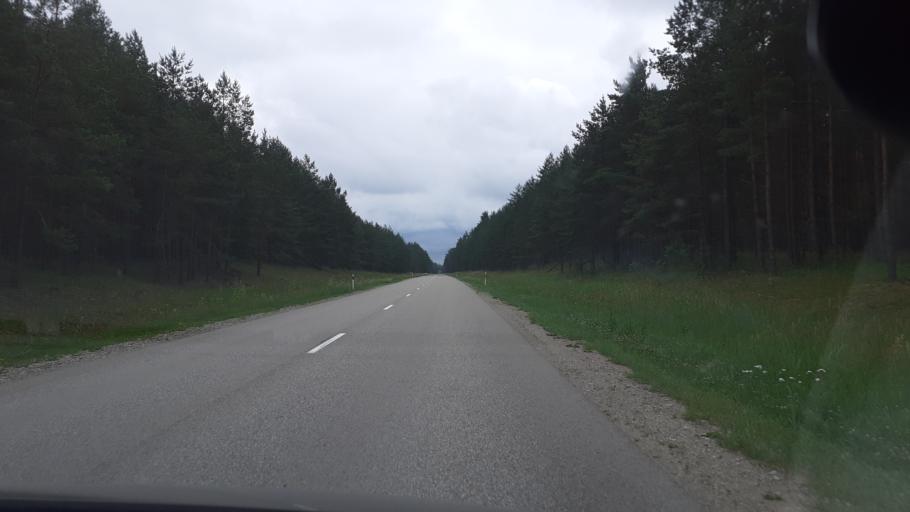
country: LV
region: Ventspils Rajons
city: Piltene
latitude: 57.1168
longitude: 21.7510
